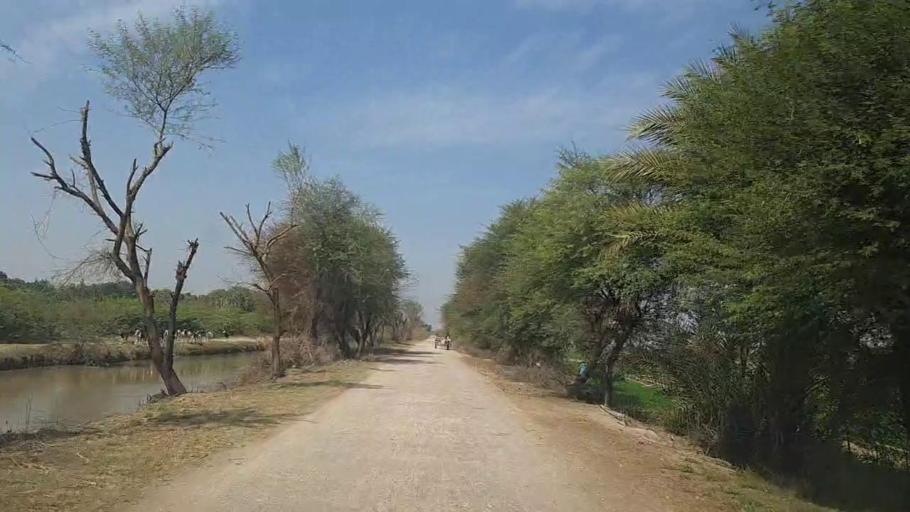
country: PK
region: Sindh
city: Mirpur Khas
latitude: 25.4894
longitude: 68.9217
